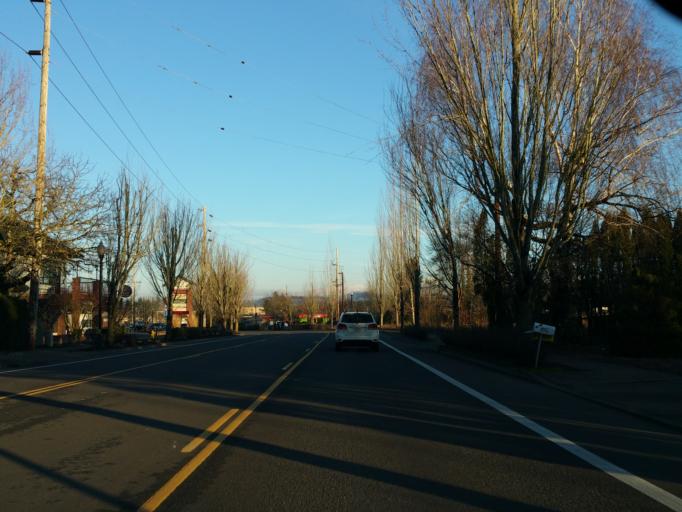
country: US
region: Oregon
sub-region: Multnomah County
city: Fairview
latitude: 45.5344
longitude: -122.4375
